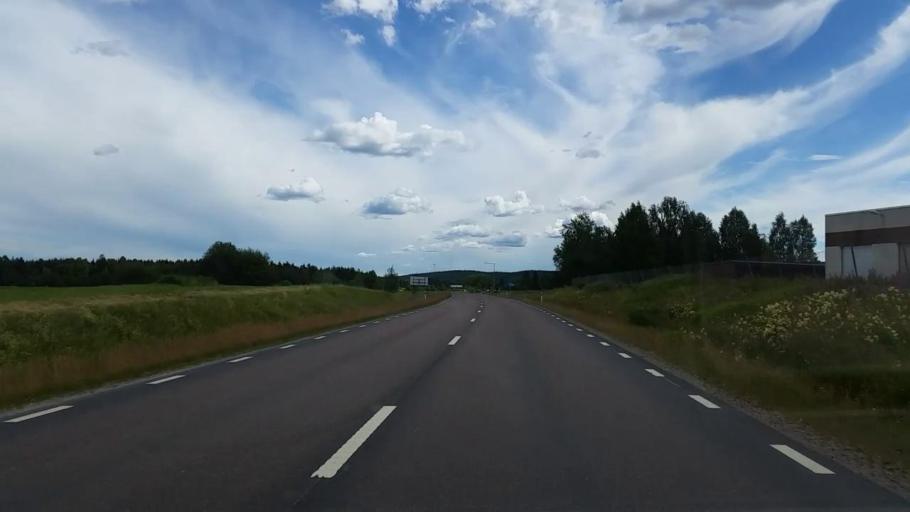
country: SE
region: Gaevleborg
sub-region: Ovanakers Kommun
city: Edsbyn
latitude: 61.3750
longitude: 15.8421
